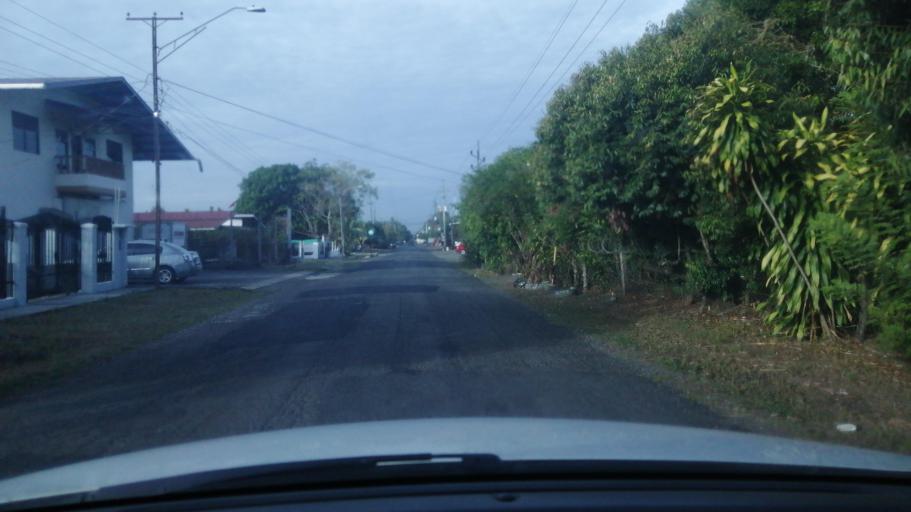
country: PA
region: Chiriqui
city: David
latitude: 8.4423
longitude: -82.4322
